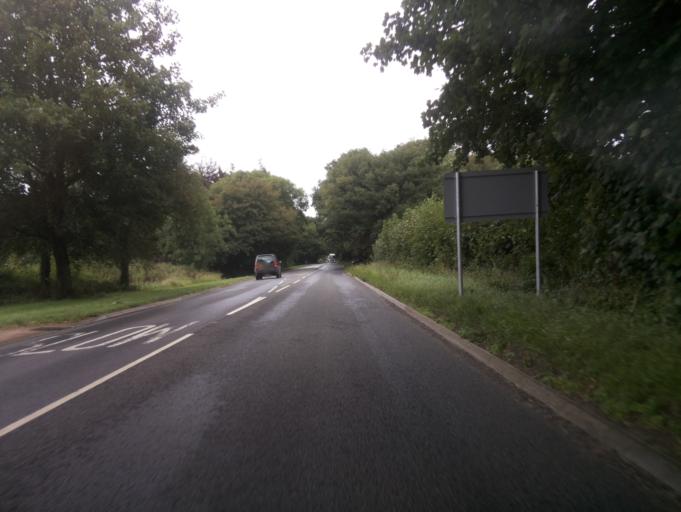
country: GB
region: England
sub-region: Devon
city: Uffculme
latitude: 50.9049
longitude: -3.3536
